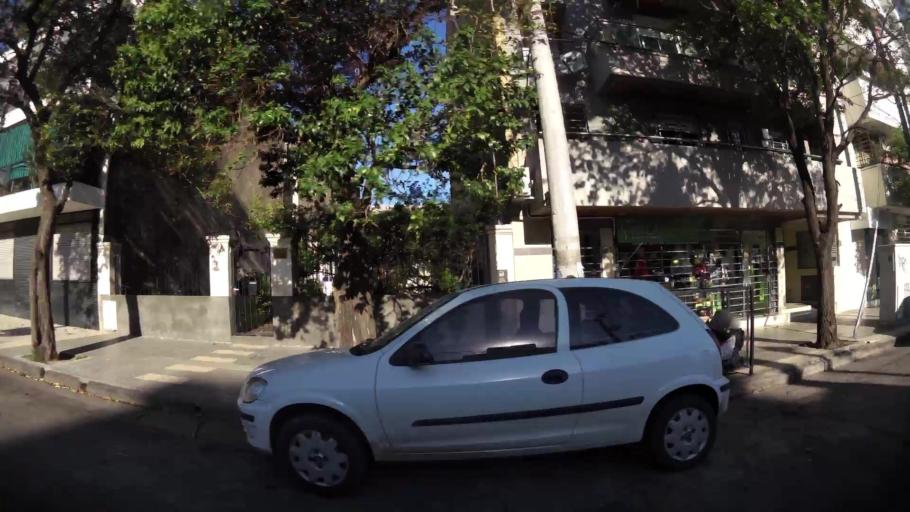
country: AR
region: Cordoba
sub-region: Departamento de Capital
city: Cordoba
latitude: -31.3896
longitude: -64.1824
